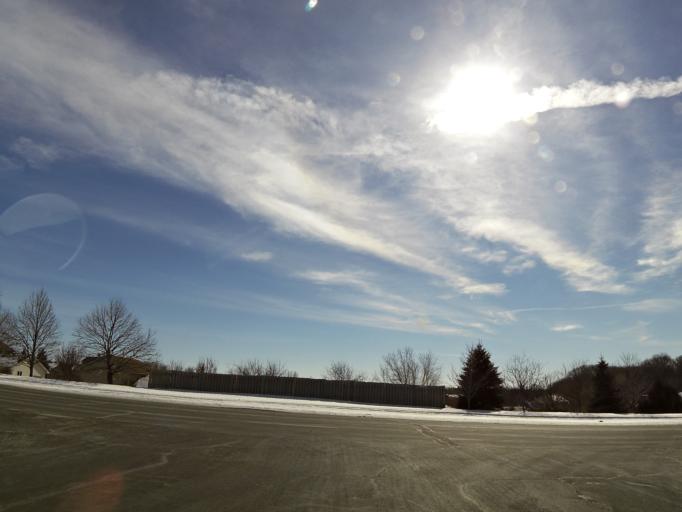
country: US
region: Minnesota
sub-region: Washington County
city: Woodbury
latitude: 44.9381
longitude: -92.9133
